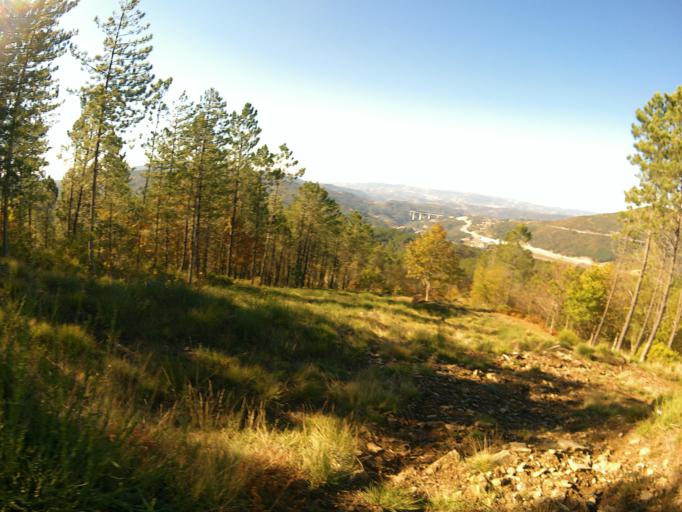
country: PT
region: Vila Real
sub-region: Mesao Frio
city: Mesao Frio
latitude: 41.2437
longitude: -7.9314
